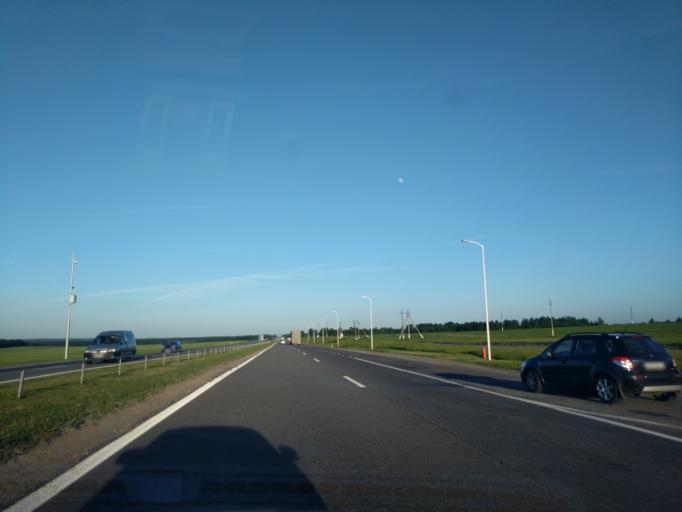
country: BY
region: Minsk
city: Ivyanyets
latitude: 54.0405
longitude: 26.8278
